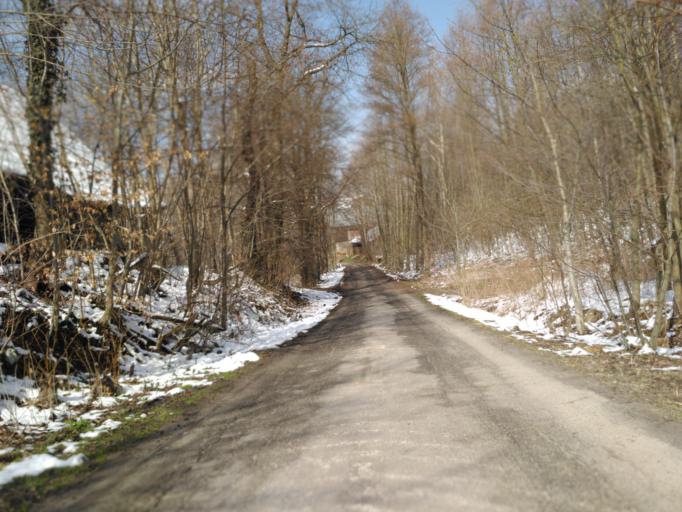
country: PL
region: Subcarpathian Voivodeship
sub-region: Powiat ropczycko-sedziszowski
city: Niedzwiada
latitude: 49.9970
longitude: 21.5812
